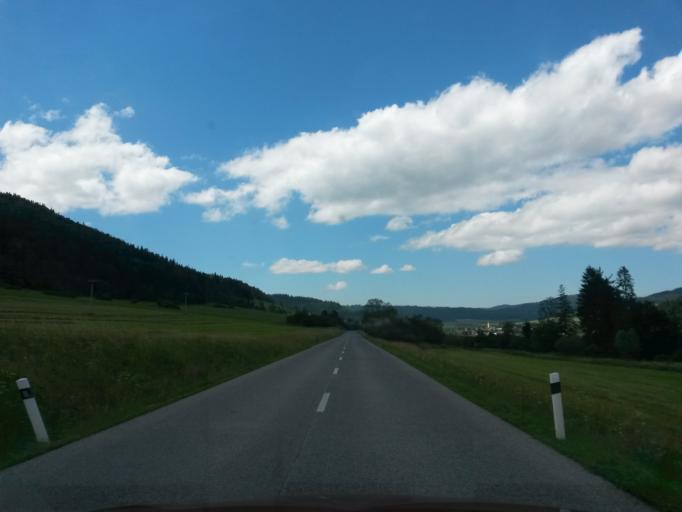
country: SK
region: Kosicky
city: Krompachy
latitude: 48.7998
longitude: 20.7387
